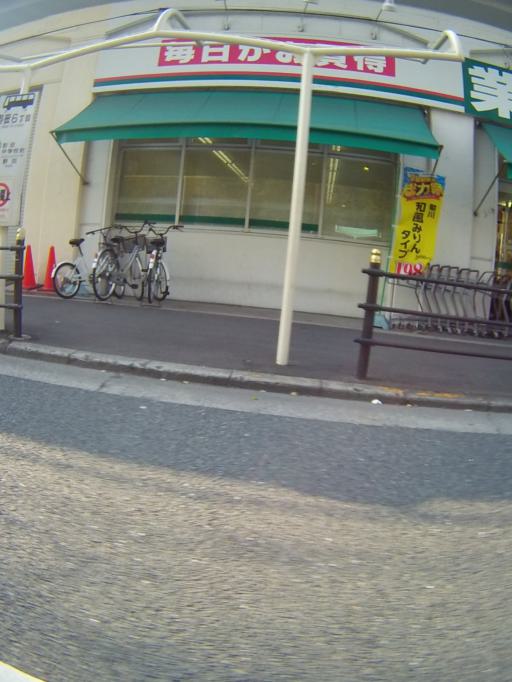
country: JP
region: Osaka
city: Osaka-shi
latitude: 34.6849
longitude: 135.4696
